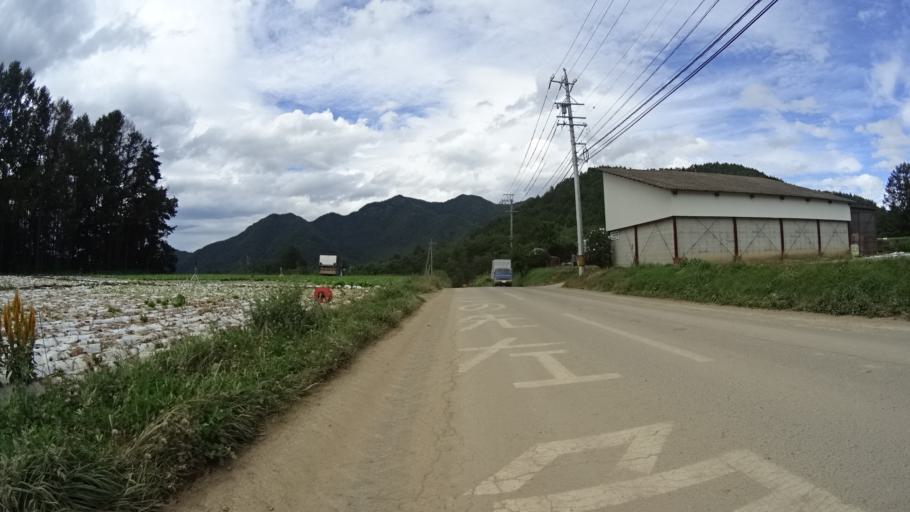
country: JP
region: Nagano
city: Saku
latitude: 35.9588
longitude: 138.5474
